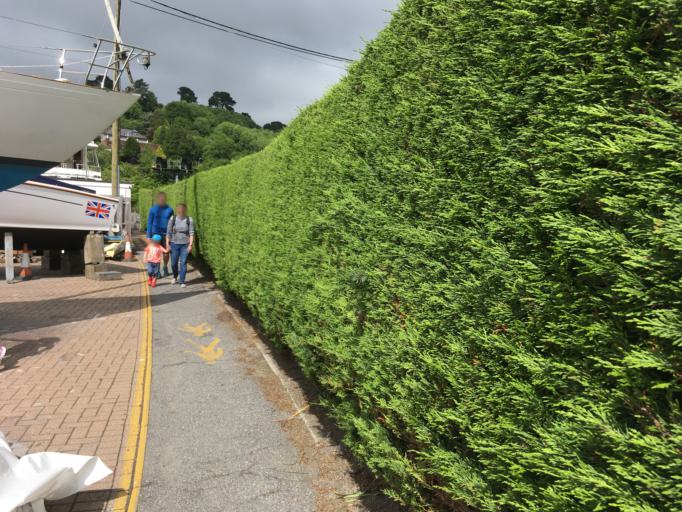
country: GB
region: England
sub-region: Devon
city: Dartmouth
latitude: 50.3502
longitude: -3.5707
